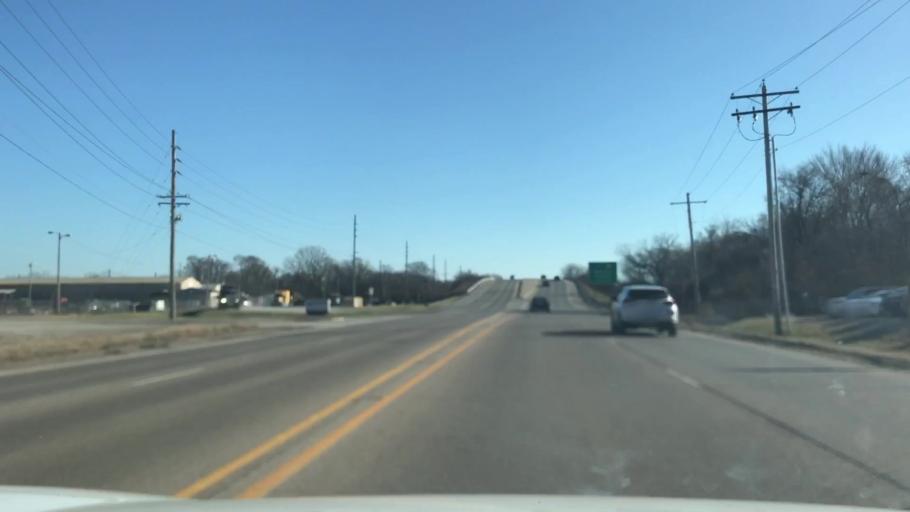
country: US
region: Illinois
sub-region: Saint Clair County
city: Alorton
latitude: 38.5959
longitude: -90.1232
